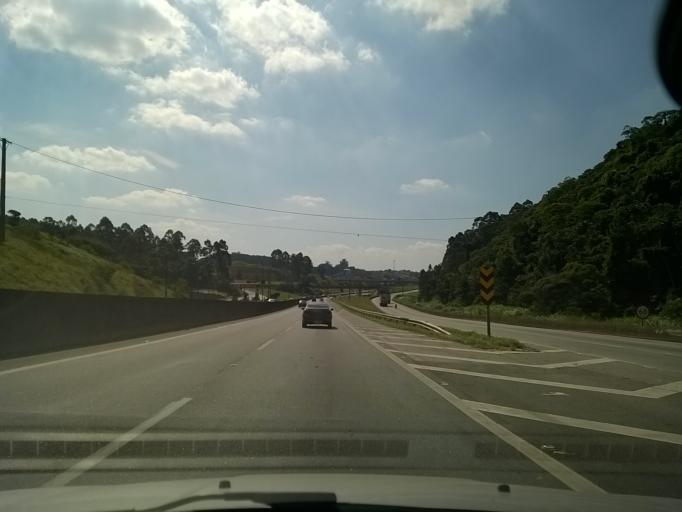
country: BR
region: Sao Paulo
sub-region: Osasco
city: Osasco
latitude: -23.4571
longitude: -46.7842
